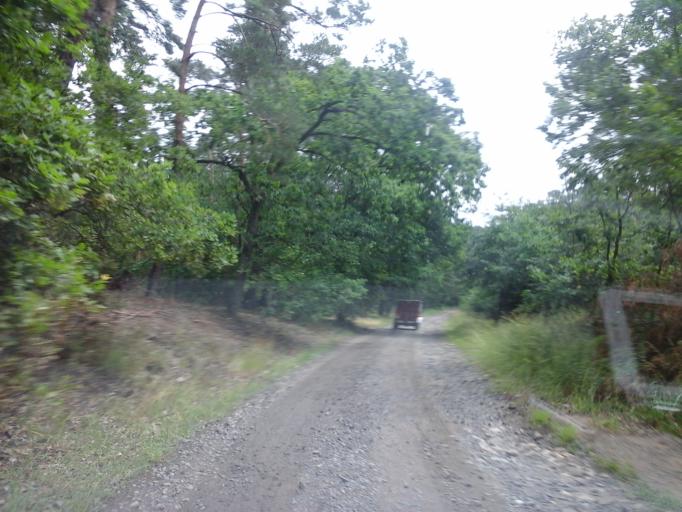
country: PL
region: West Pomeranian Voivodeship
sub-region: Powiat choszczenski
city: Bierzwnik
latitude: 52.9756
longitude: 15.6093
